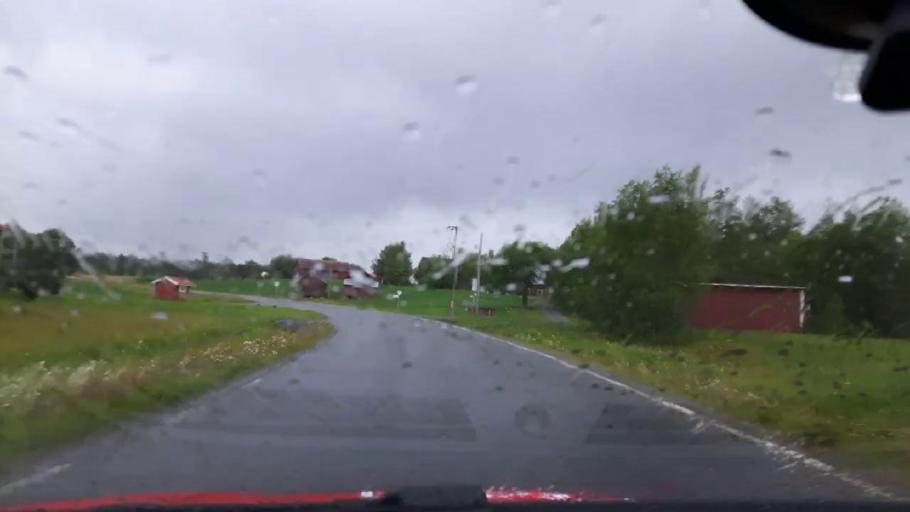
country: SE
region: Jaemtland
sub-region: OEstersunds Kommun
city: Brunflo
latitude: 63.0103
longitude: 14.7309
